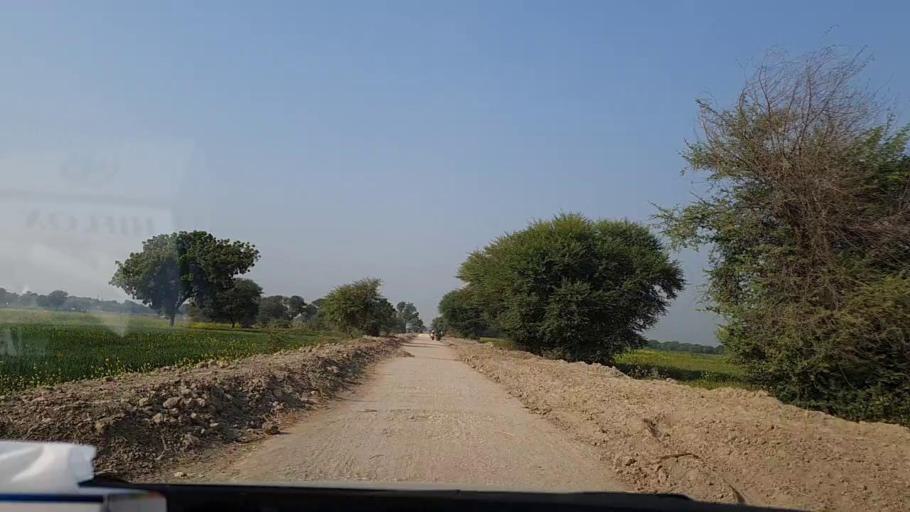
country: PK
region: Sindh
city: Tando Ghulam Ali
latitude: 25.1752
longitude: 68.8768
